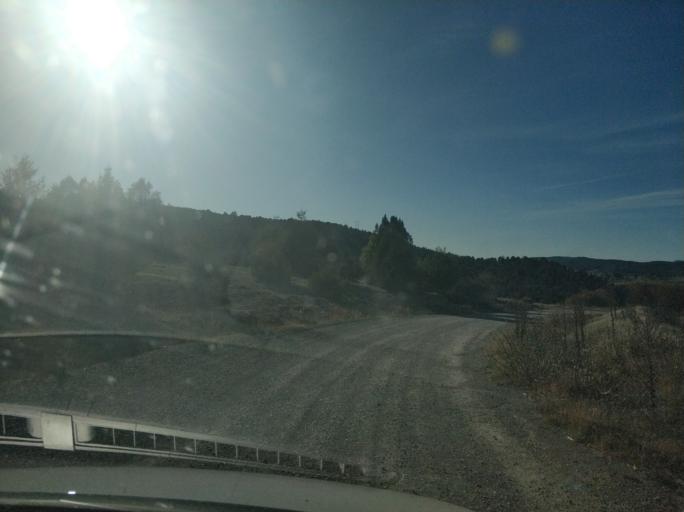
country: ES
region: Castille and Leon
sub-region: Provincia de Burgos
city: Hontoria del Pinar
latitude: 41.8415
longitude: -3.1639
